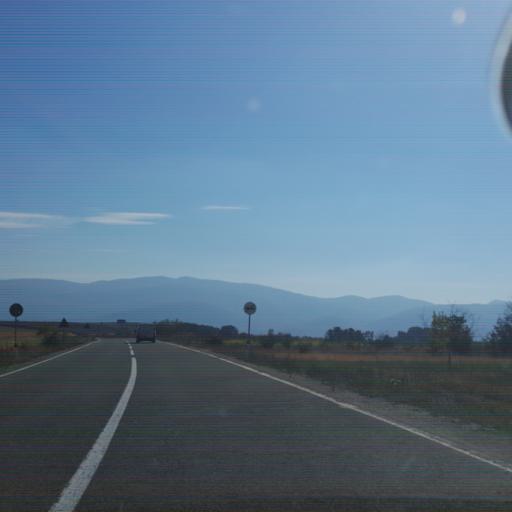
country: RS
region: Central Serbia
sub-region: Nisavski Okrug
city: Svrljig
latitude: 43.4499
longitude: 22.1710
